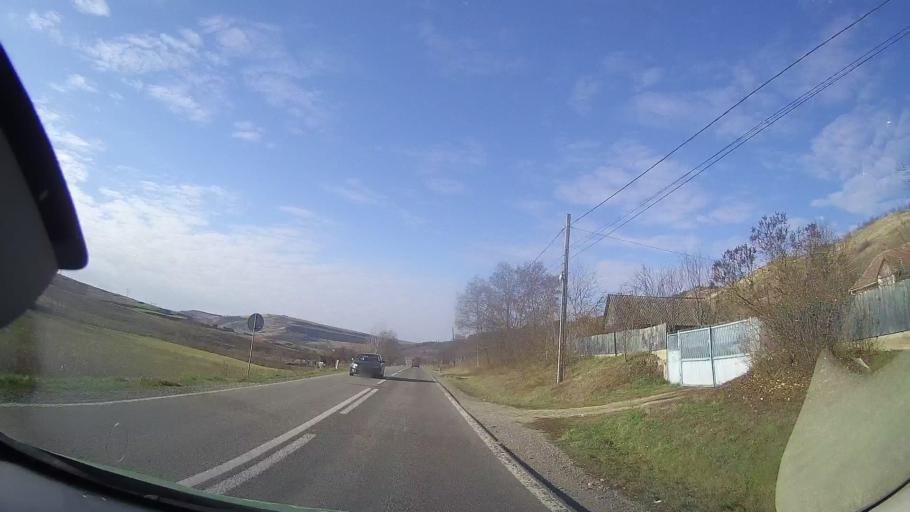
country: RO
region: Cluj
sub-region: Comuna Caianu
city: Vaida-Camaras
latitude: 46.7985
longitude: 23.9475
